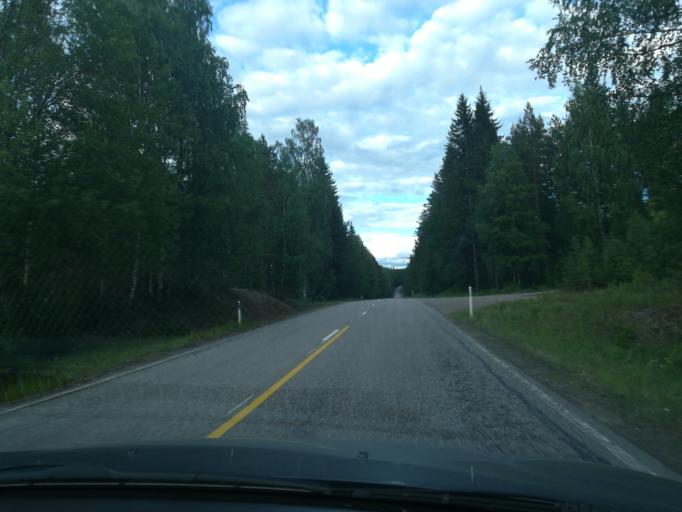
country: FI
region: Southern Savonia
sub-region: Mikkeli
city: Puumala
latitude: 61.5680
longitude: 28.0552
